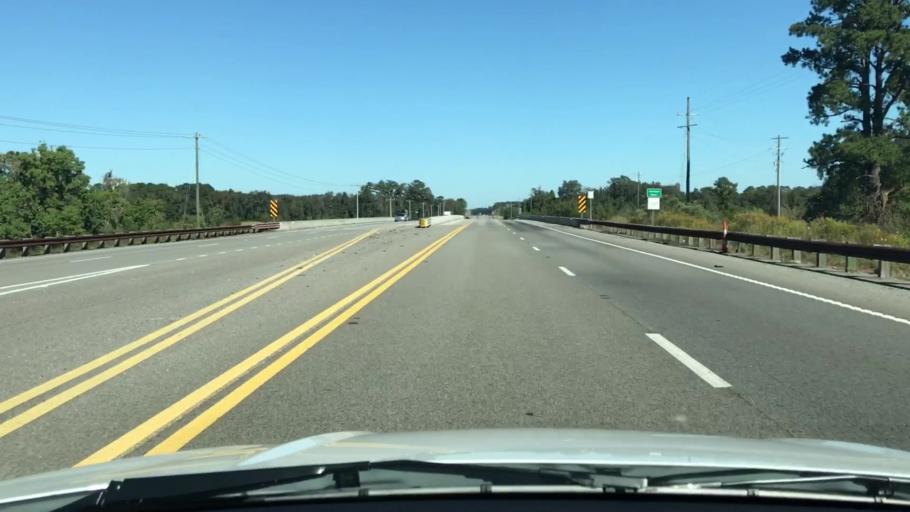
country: US
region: South Carolina
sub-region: Colleton County
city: Walterboro
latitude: 32.7432
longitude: -80.5575
